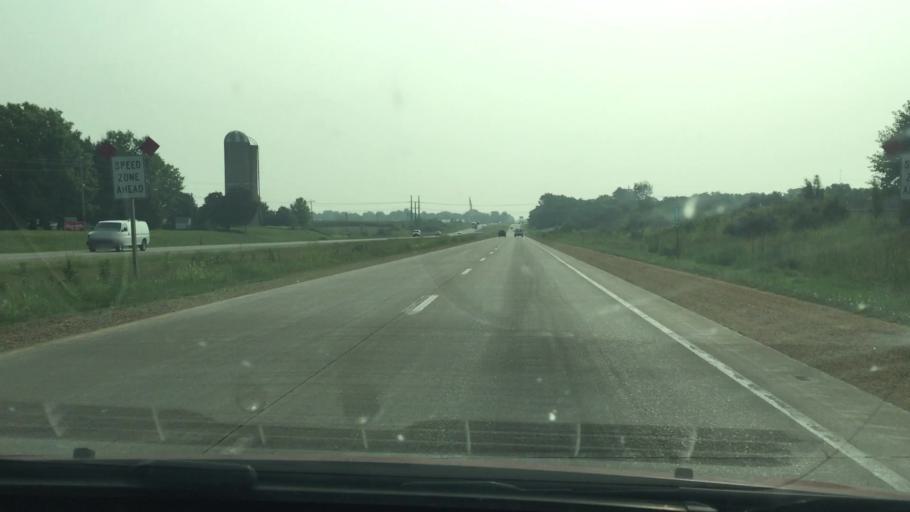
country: US
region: Iowa
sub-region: Scott County
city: Buffalo
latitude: 41.5088
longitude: -90.7063
